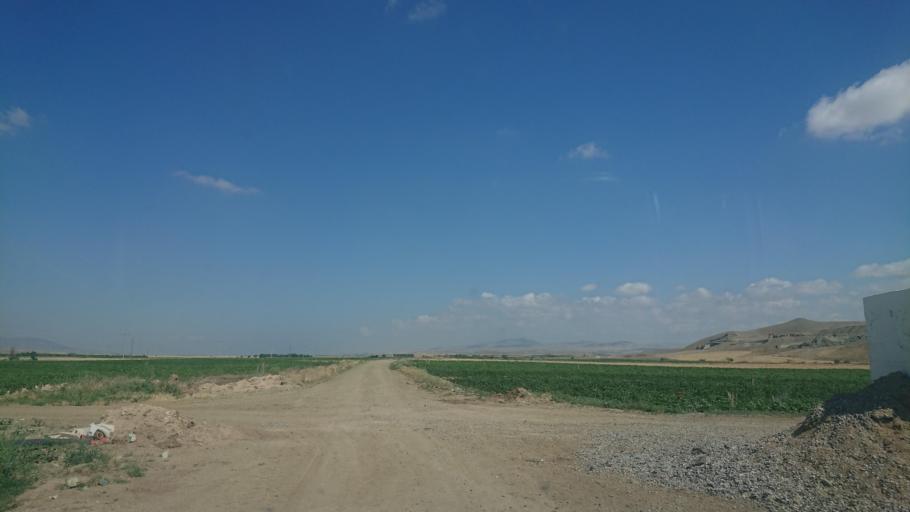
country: TR
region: Aksaray
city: Sariyahsi
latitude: 38.9743
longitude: 33.9147
